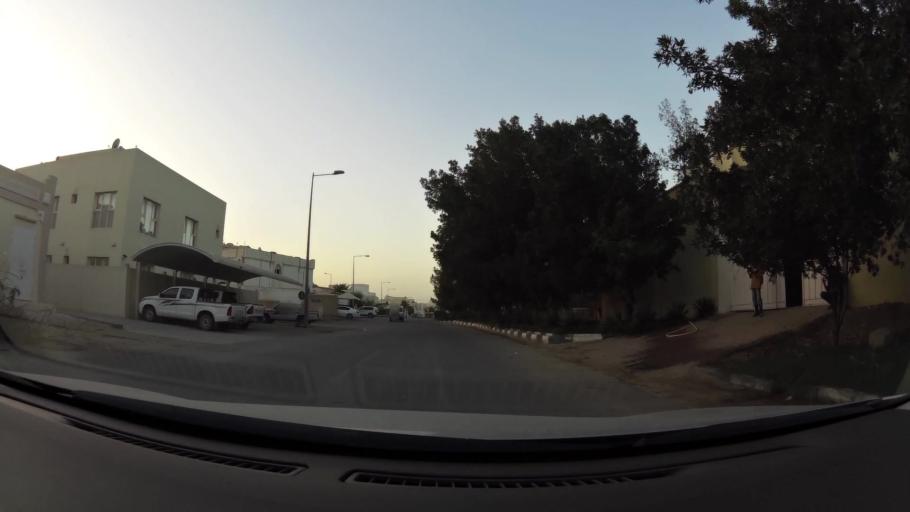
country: QA
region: Baladiyat ar Rayyan
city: Ar Rayyan
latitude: 25.3232
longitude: 51.4645
